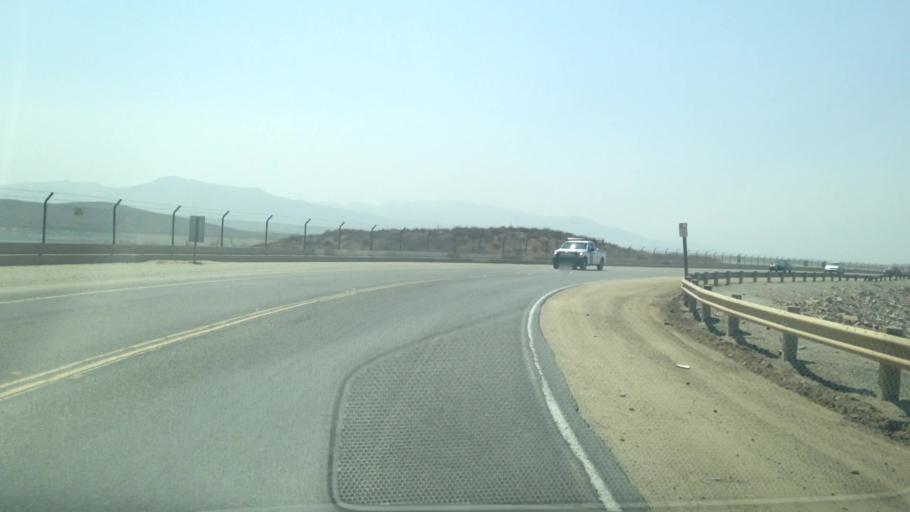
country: US
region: California
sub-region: Riverside County
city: El Cerrito
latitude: 33.8409
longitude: -117.4612
